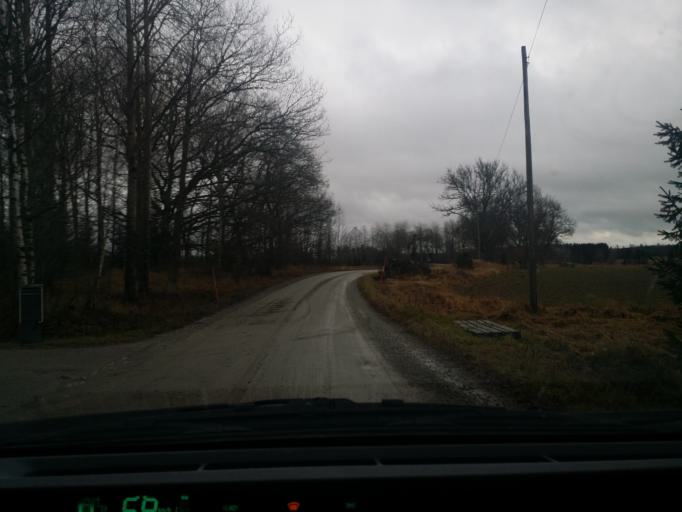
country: SE
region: Vaestmanland
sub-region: Vasteras
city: Skultuna
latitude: 59.7807
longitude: 16.3912
